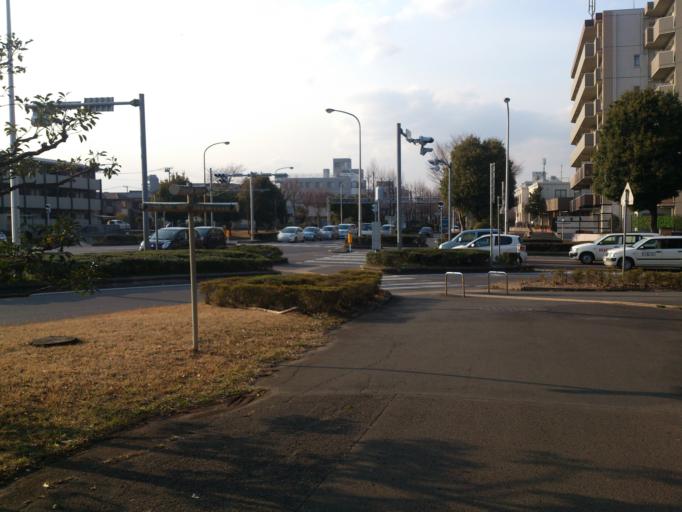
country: JP
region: Ibaraki
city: Naka
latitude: 36.0871
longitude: 140.1036
